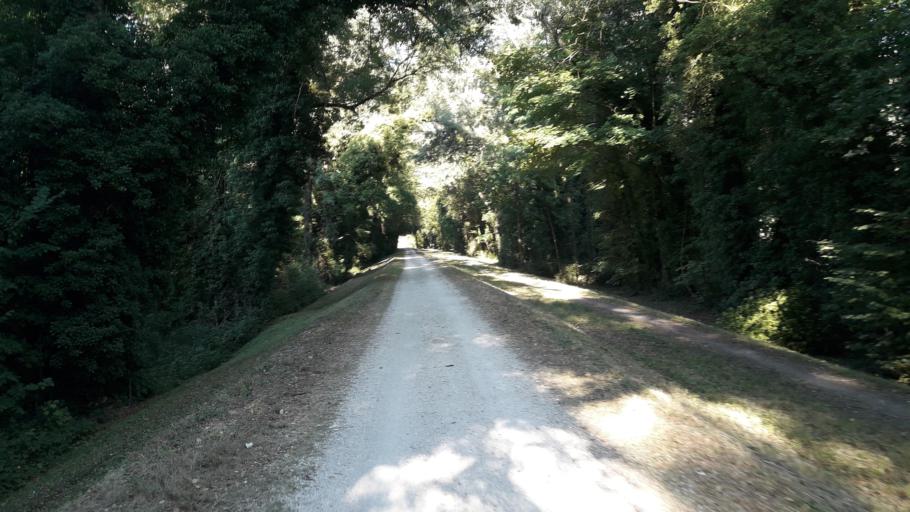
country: FR
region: Rhone-Alpes
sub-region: Departement de l'Isere
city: Gieres
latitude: 45.1900
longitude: 5.7906
